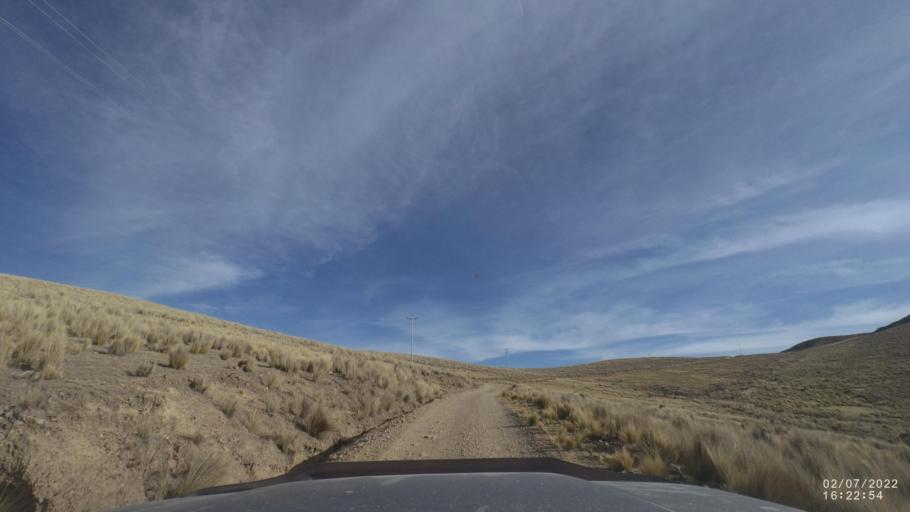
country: BO
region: Cochabamba
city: Irpa Irpa
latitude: -17.9372
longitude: -66.4567
